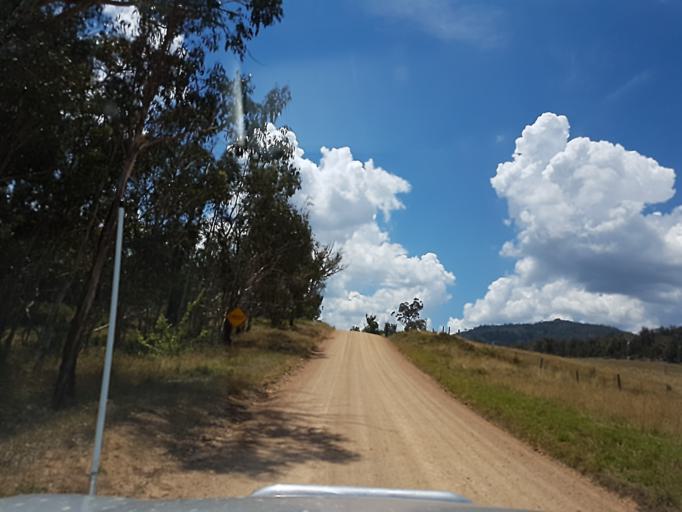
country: AU
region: Victoria
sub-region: Alpine
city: Mount Beauty
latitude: -36.8989
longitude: 147.8735
